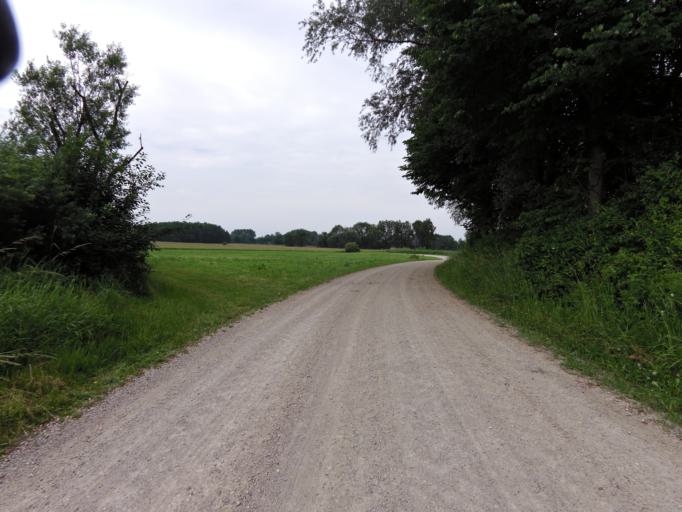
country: DE
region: Bavaria
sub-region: Upper Bavaria
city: Langenbach
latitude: 48.4496
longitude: 11.8938
